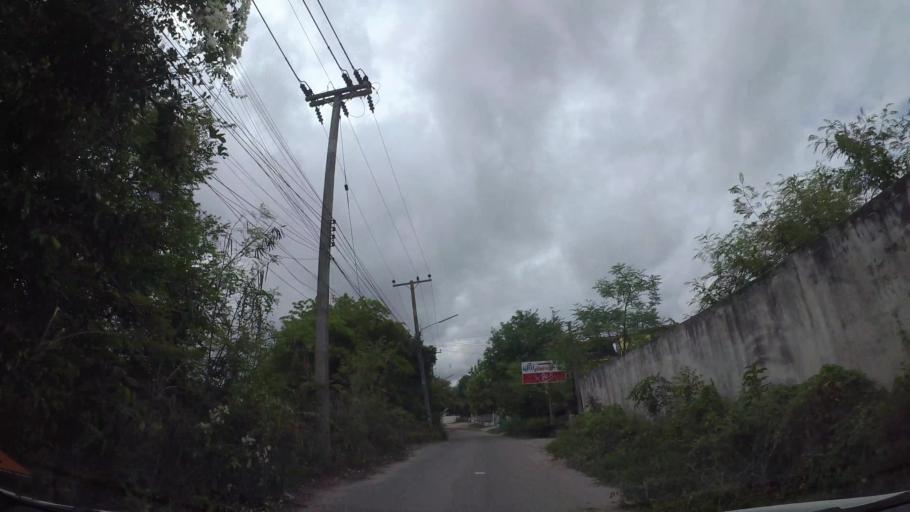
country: TH
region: Rayong
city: Rayong
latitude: 12.6669
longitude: 101.2584
